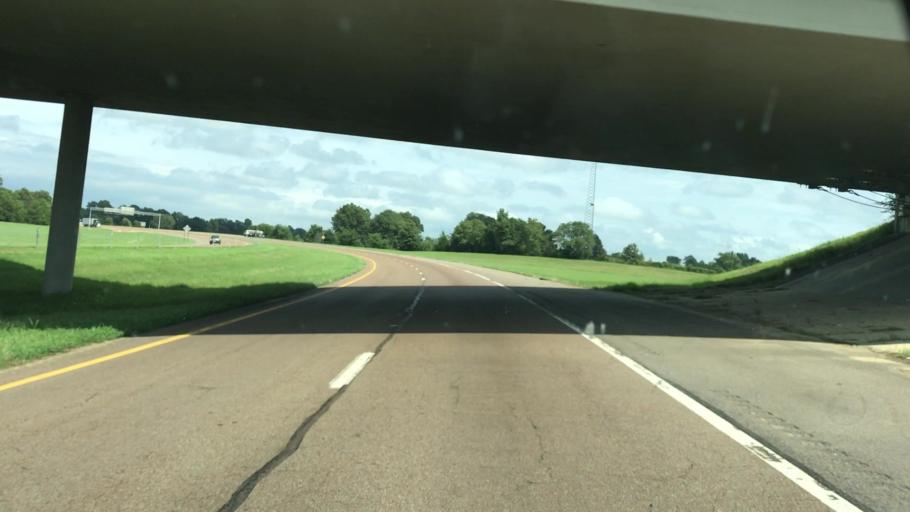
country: US
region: Tennessee
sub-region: Obion County
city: Union City
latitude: 36.4435
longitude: -89.0126
